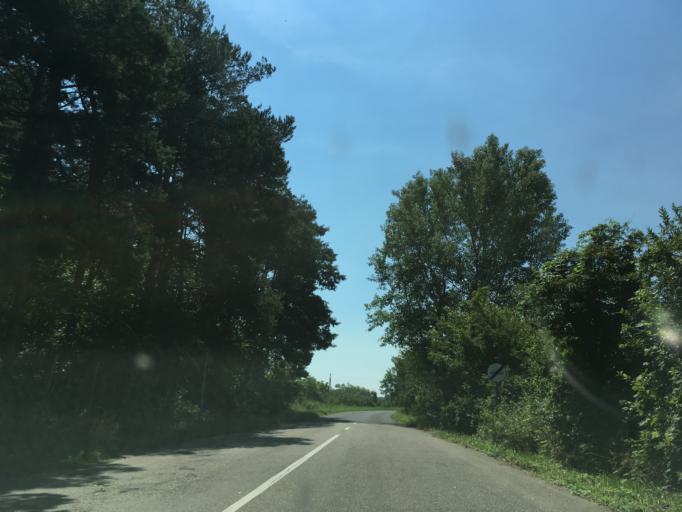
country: HU
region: Hajdu-Bihar
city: Mikepercs
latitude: 47.4825
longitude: 21.7122
